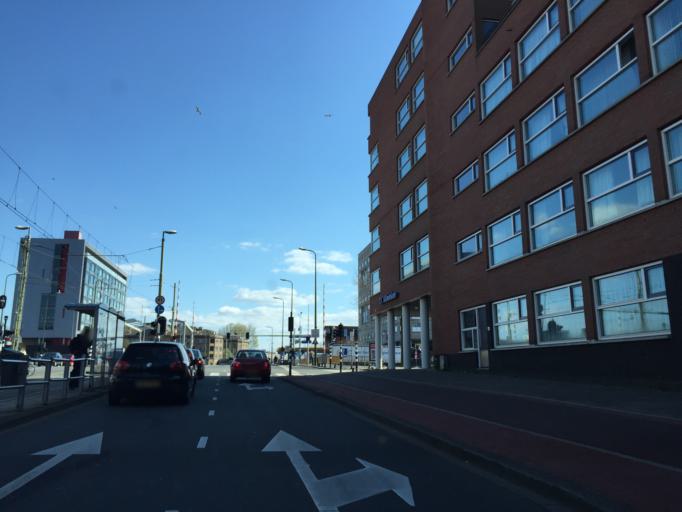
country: NL
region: South Holland
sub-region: Gemeente Den Haag
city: The Hague
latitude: 52.0681
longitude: 4.3277
